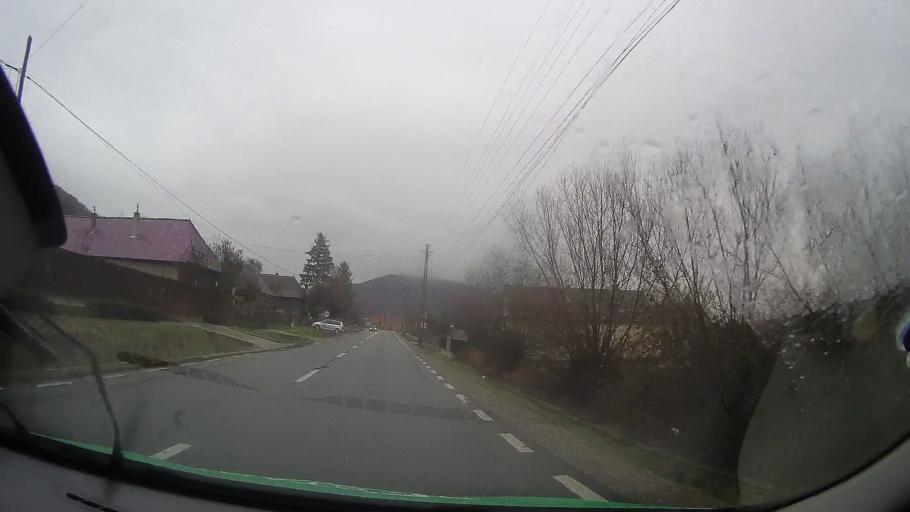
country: RO
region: Bistrita-Nasaud
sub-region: Comuna Galatii Bistritei
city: Galatii Bistritei
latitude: 46.9835
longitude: 24.4296
